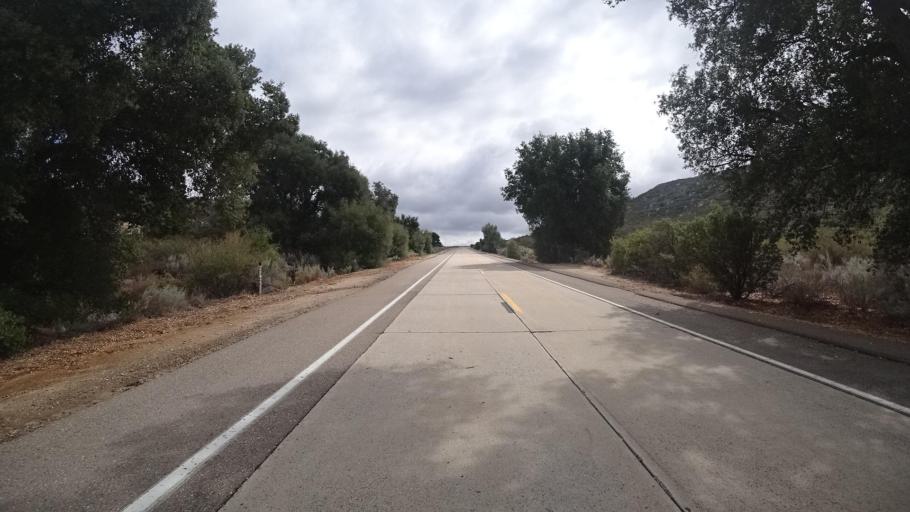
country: US
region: California
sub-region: San Diego County
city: Pine Valley
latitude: 32.7274
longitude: -116.4805
